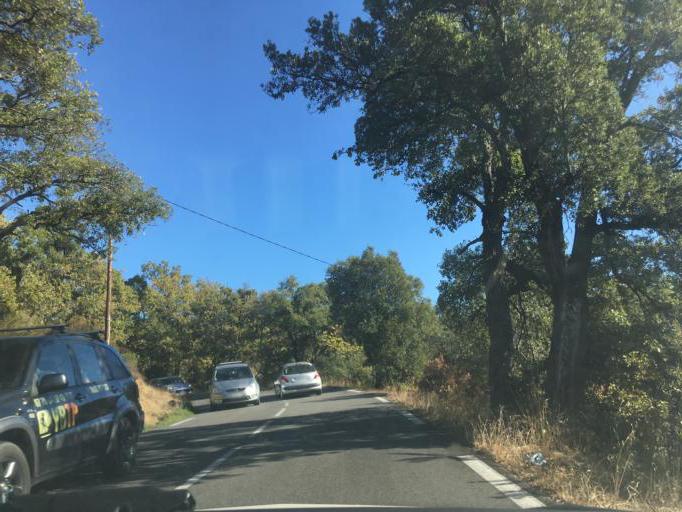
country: FR
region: Provence-Alpes-Cote d'Azur
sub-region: Departement du Var
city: La Garde-Freinet
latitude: 43.3277
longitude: 6.4657
